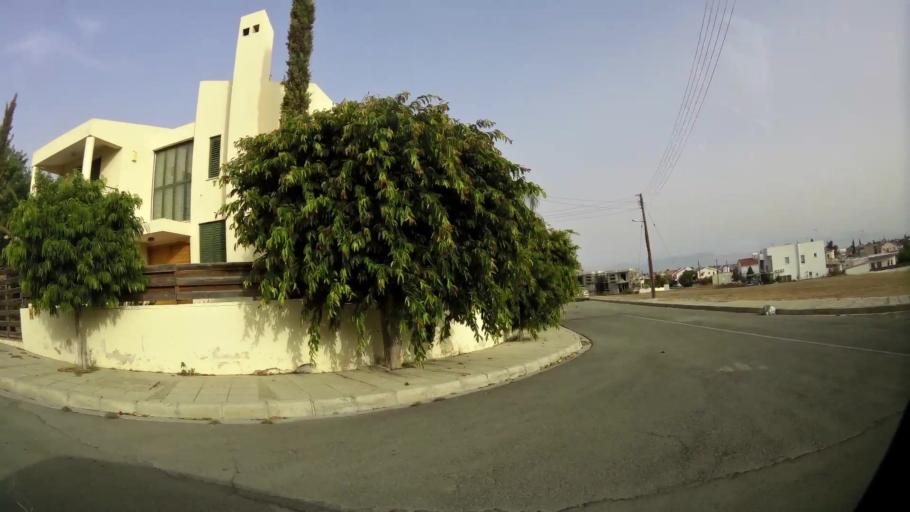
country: CY
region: Lefkosia
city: Dali
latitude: 35.0623
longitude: 33.3954
